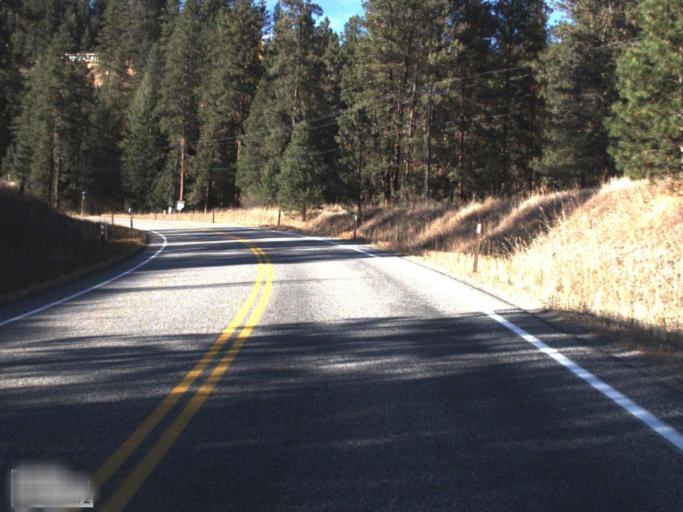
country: CA
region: British Columbia
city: Rossland
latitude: 48.9449
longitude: -117.7722
